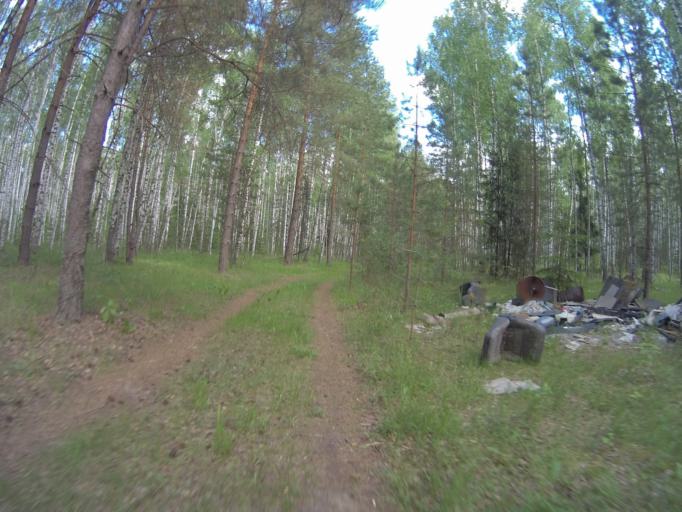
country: RU
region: Vladimir
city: Raduzhnyy
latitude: 55.9970
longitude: 40.2718
